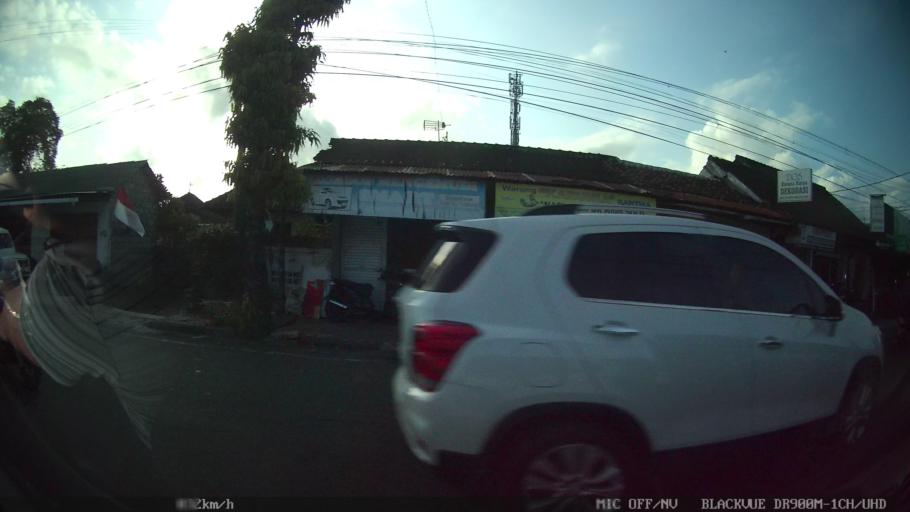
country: ID
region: Bali
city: Banjar Kertasari
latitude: -8.6193
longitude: 115.2113
